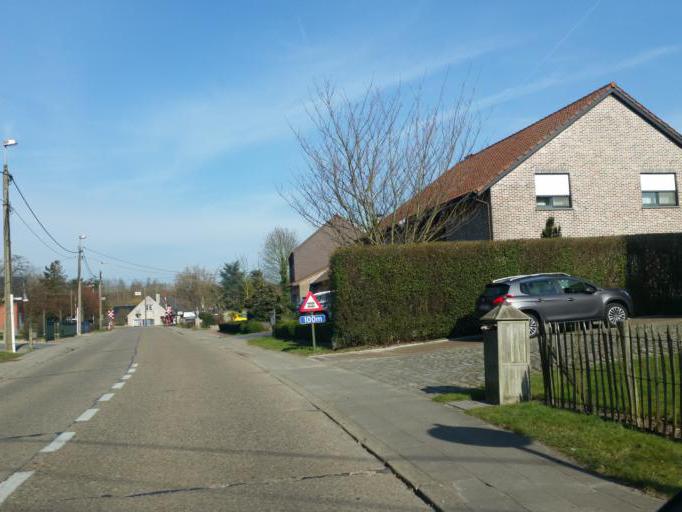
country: BE
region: Flanders
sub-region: Provincie Vlaams-Brabant
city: Boortmeerbeek
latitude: 50.9880
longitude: 4.5569
